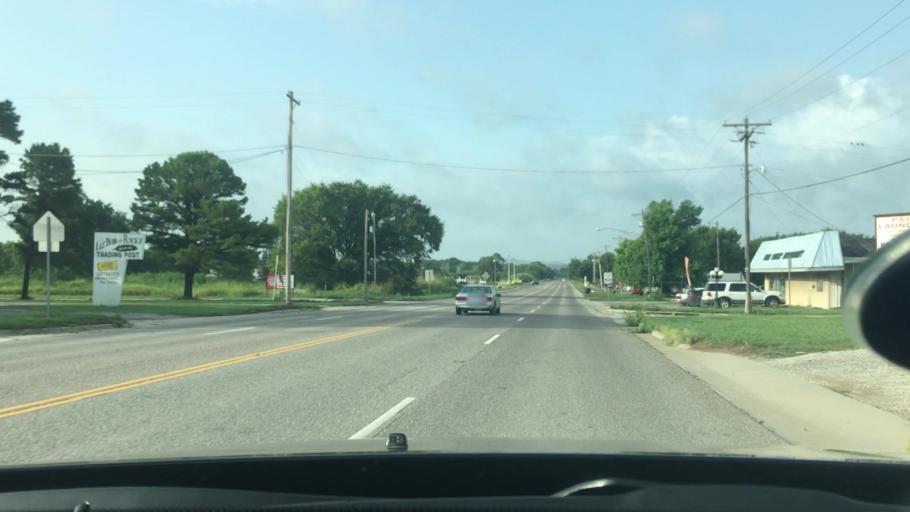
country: US
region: Oklahoma
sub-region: Murray County
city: Davis
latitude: 34.4985
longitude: -97.1257
